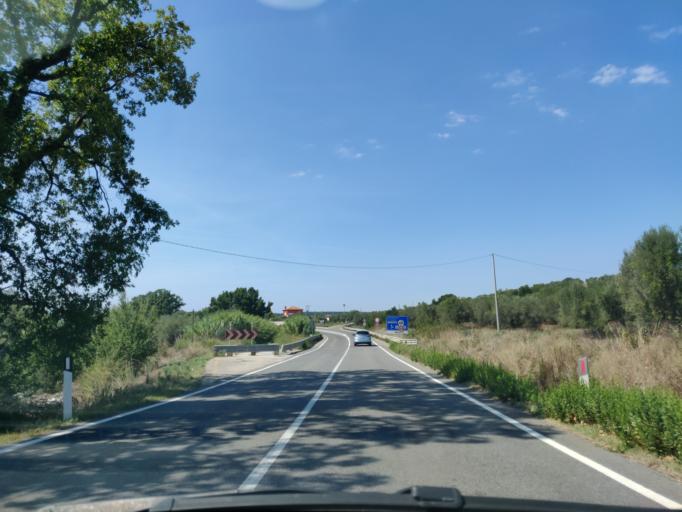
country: IT
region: Latium
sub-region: Provincia di Viterbo
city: Monte Romano
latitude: 42.2634
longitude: 11.8680
